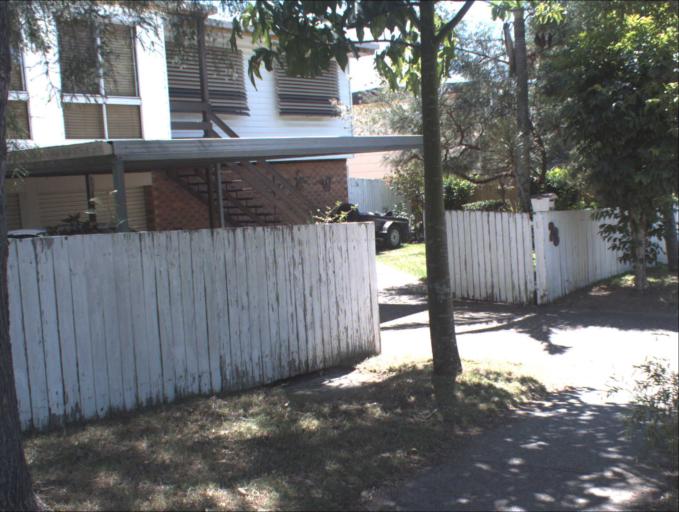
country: AU
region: Queensland
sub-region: Logan
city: Logan City
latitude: -27.6446
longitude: 153.1208
